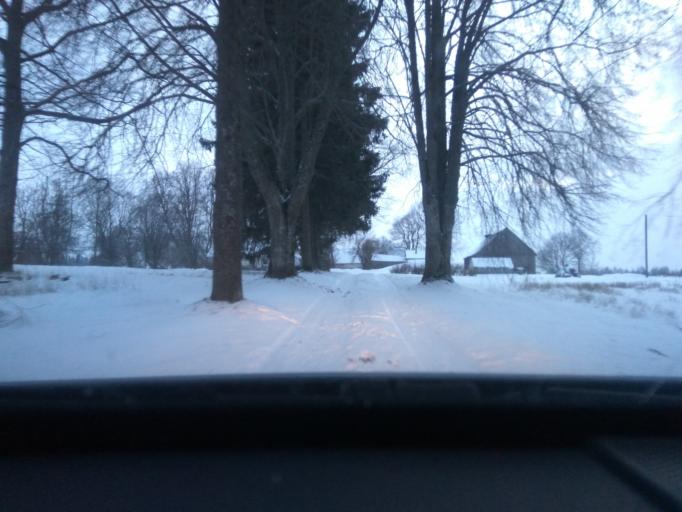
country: LV
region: Kuldigas Rajons
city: Kuldiga
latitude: 56.8619
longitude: 21.8046
